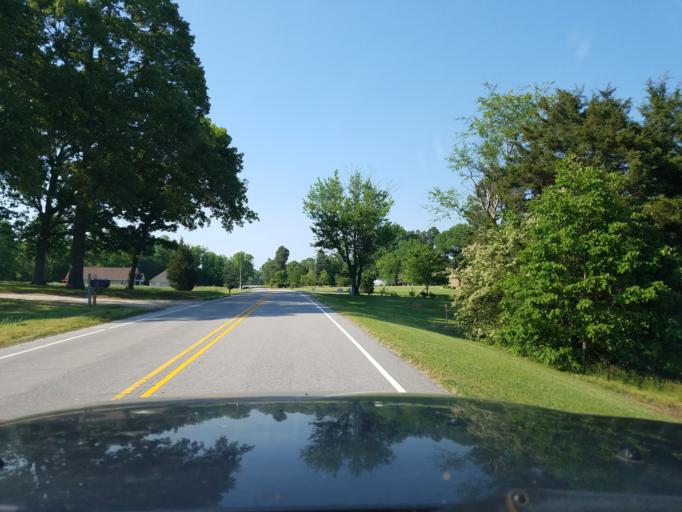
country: US
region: North Carolina
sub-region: Vance County
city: Henderson
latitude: 36.3975
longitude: -78.3683
